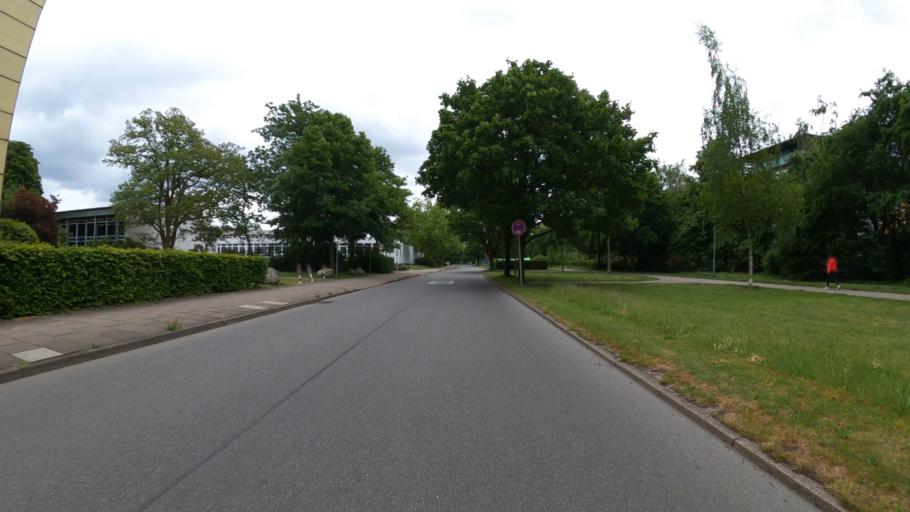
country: DE
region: Schleswig-Holstein
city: Norderstedt
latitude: 53.6888
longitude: 9.9859
